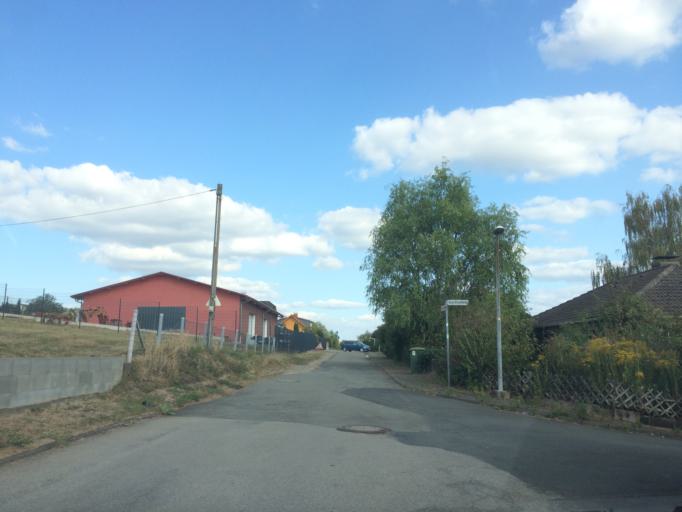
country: DE
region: North Rhine-Westphalia
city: Beverungen
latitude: 51.6116
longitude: 9.3739
